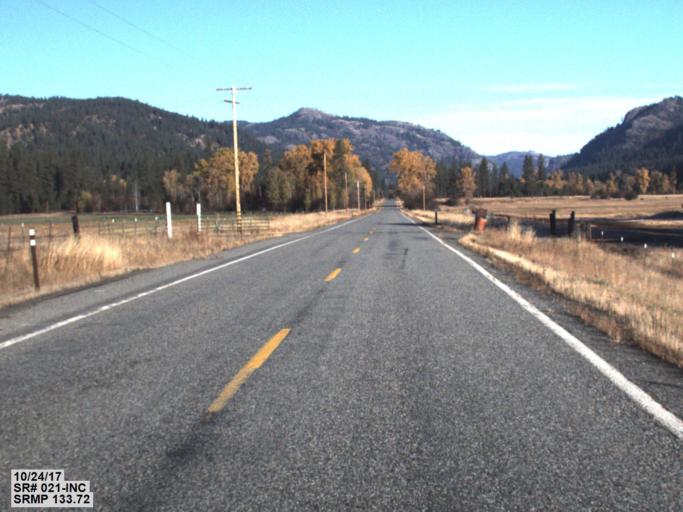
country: US
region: Washington
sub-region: Ferry County
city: Republic
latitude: 48.3026
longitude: -118.7359
